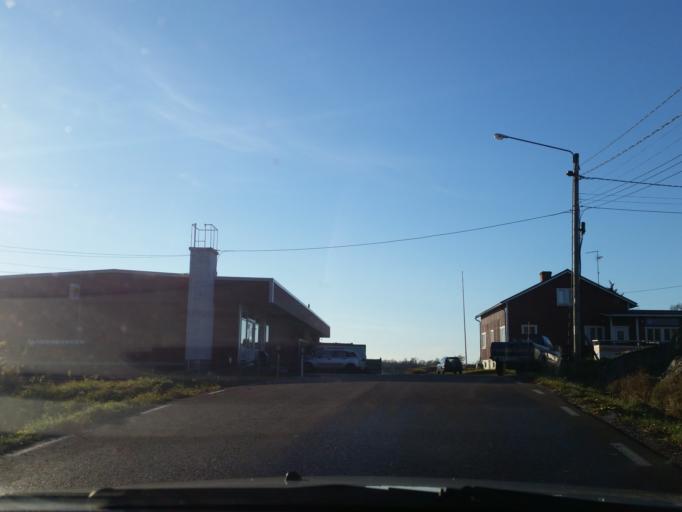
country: AX
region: Alands skaergard
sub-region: Braendoe
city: Braendoe
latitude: 60.4124
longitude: 21.0387
